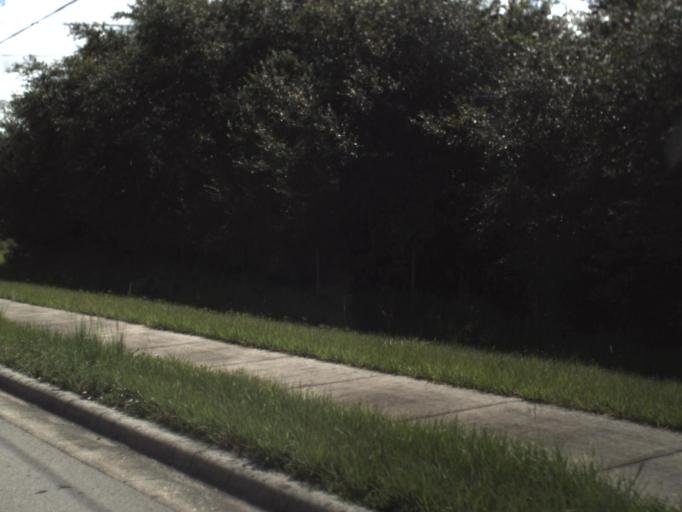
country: US
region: Florida
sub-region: Charlotte County
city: Cleveland
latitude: 26.9666
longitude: -81.9710
